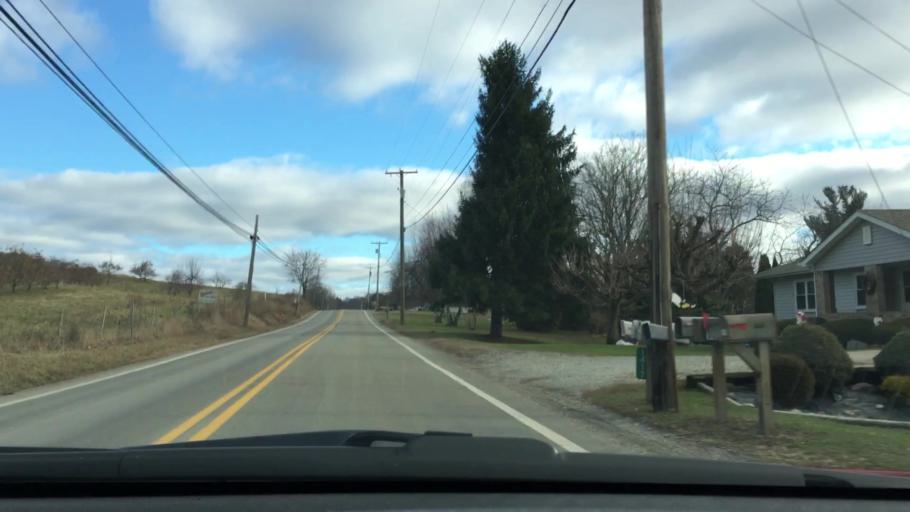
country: US
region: Pennsylvania
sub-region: Armstrong County
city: Orchard Hills
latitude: 40.6009
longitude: -79.5070
